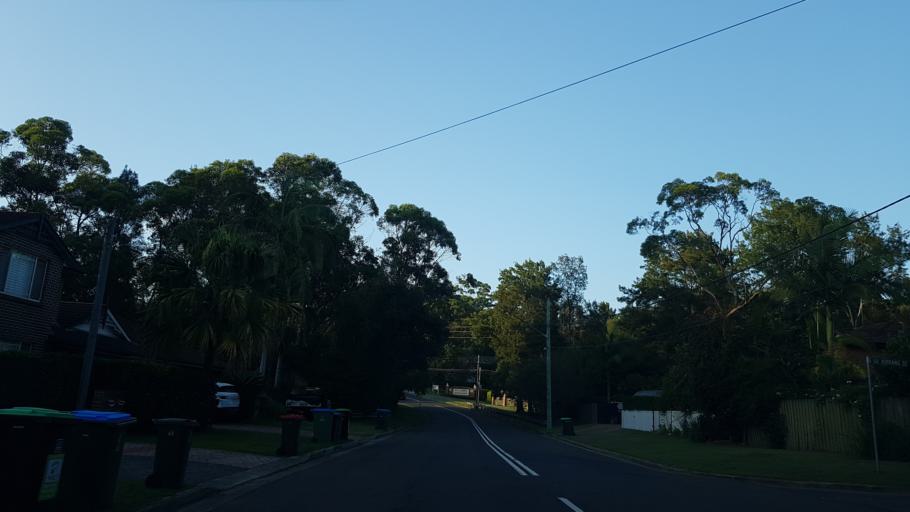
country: AU
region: New South Wales
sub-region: Warringah
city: Narraweena
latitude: -33.7401
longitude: 151.2687
